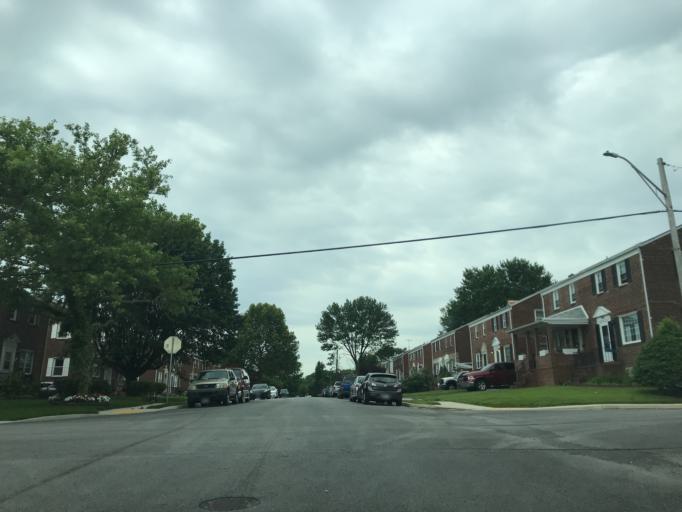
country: US
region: Maryland
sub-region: Baltimore County
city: Overlea
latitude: 39.3584
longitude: -76.5143
